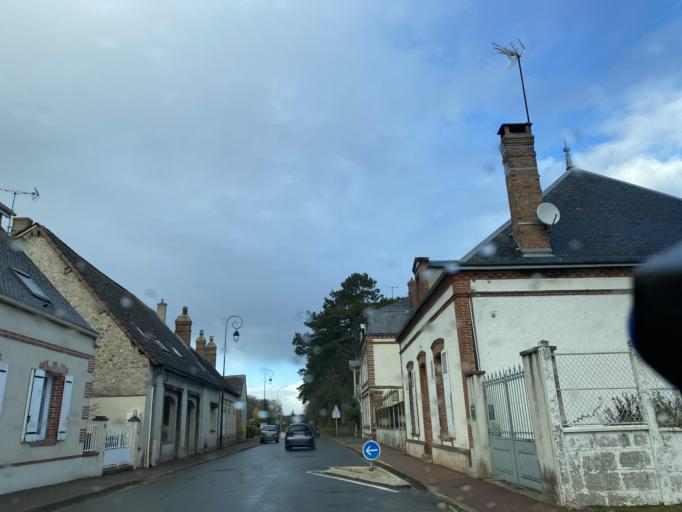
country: FR
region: Centre
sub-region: Departement d'Eure-et-Loir
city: Chateauneuf-en-Thymerais
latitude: 48.5849
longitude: 1.2390
